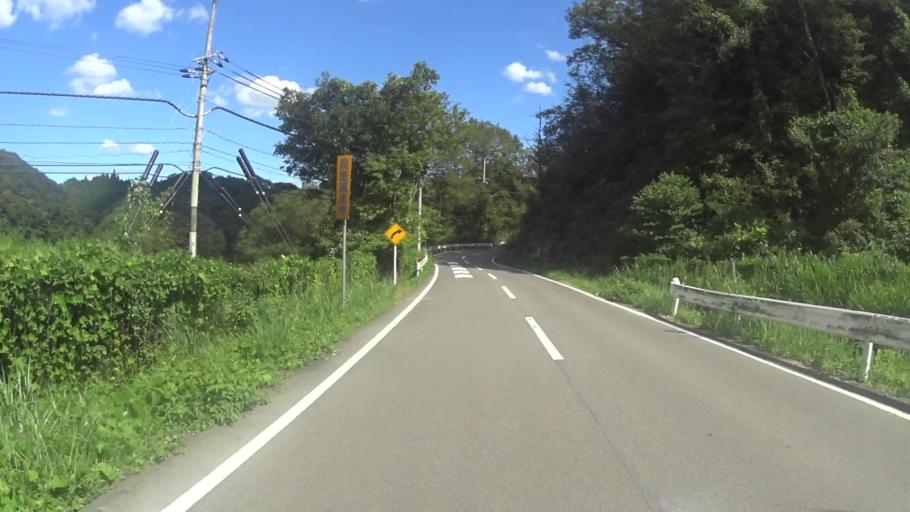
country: JP
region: Mie
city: Ueno-ebisumachi
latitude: 34.7484
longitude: 136.0105
